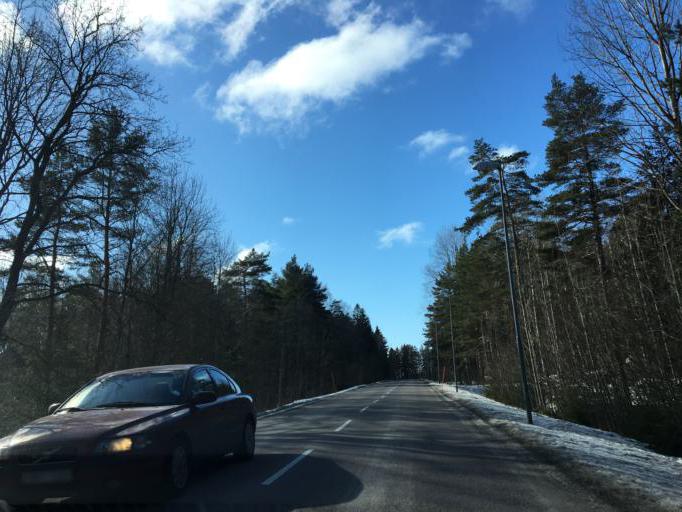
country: SE
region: Vaestmanland
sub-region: Vasteras
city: Vasteras
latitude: 59.6055
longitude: 16.4598
